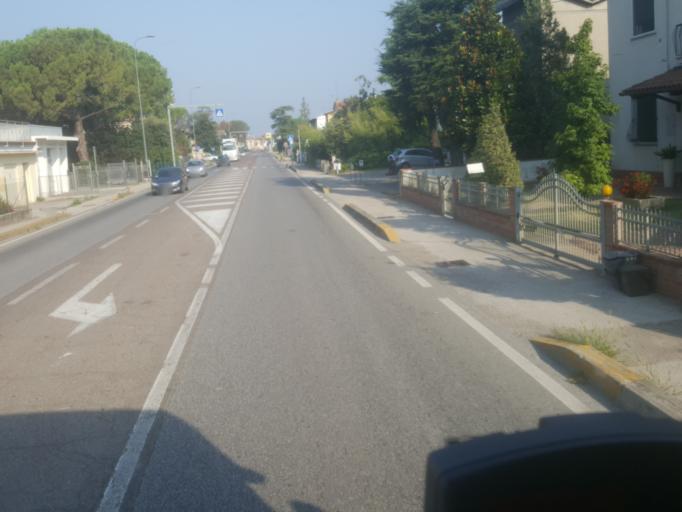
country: IT
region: Emilia-Romagna
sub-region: Provincia di Ravenna
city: Mezzano
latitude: 44.4648
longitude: 12.0903
